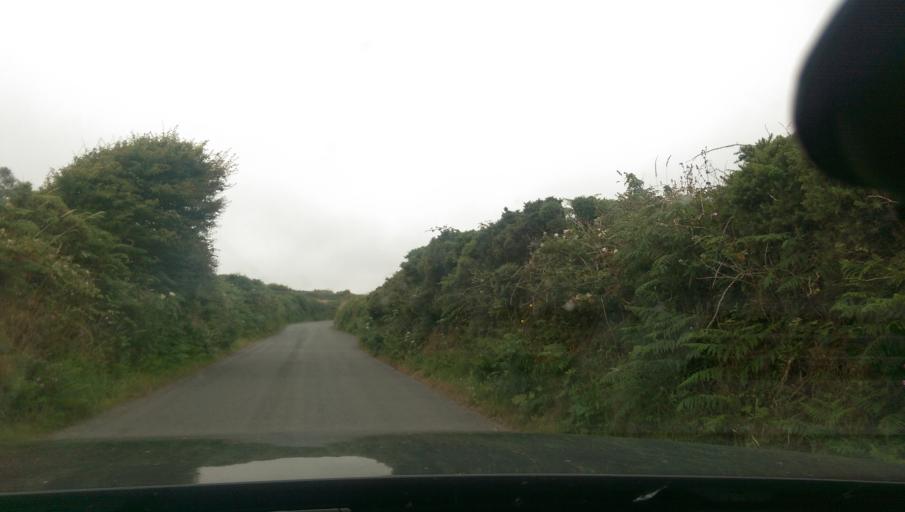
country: GB
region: England
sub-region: Cornwall
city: St. Buryan
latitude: 50.0955
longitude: -5.6487
